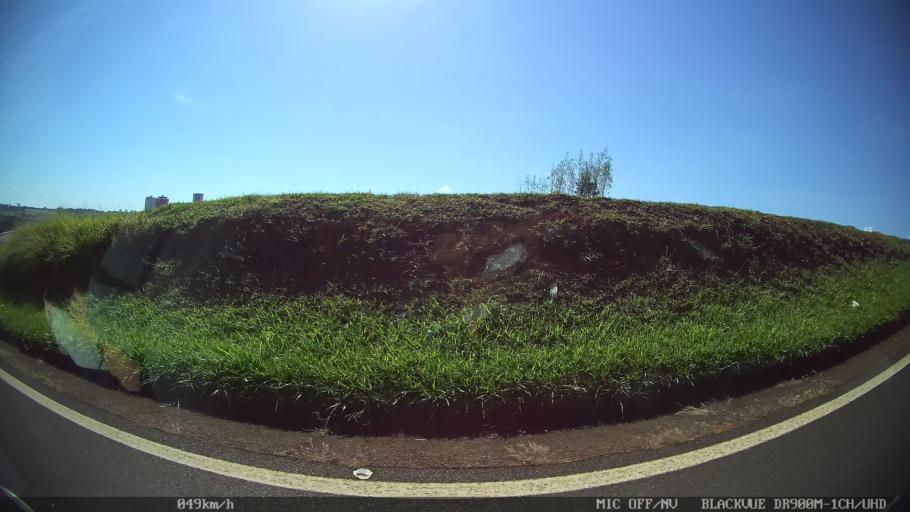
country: BR
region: Sao Paulo
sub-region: Franca
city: Franca
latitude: -20.5632
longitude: -47.4133
